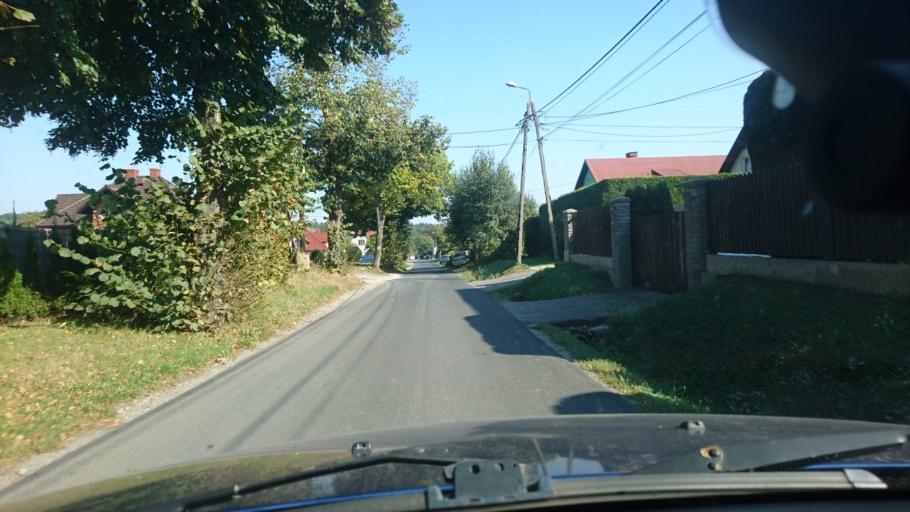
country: PL
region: Silesian Voivodeship
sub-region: Bielsko-Biala
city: Bielsko-Biala
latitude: 49.8576
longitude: 19.0587
